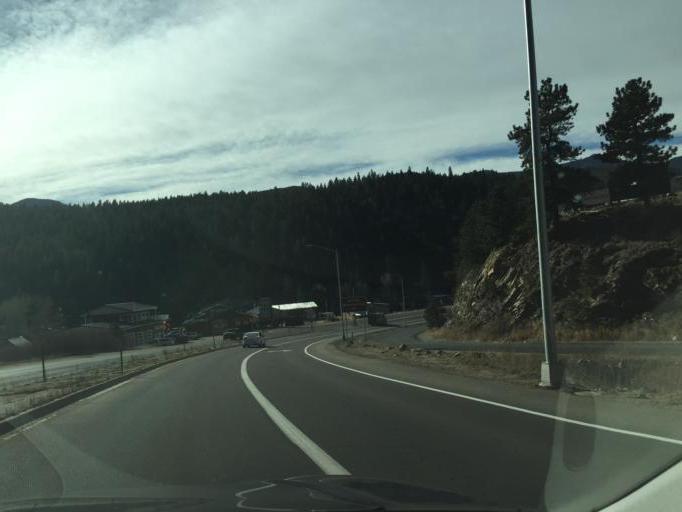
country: US
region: Colorado
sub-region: Jefferson County
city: Evergreen
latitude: 39.4069
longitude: -105.4730
